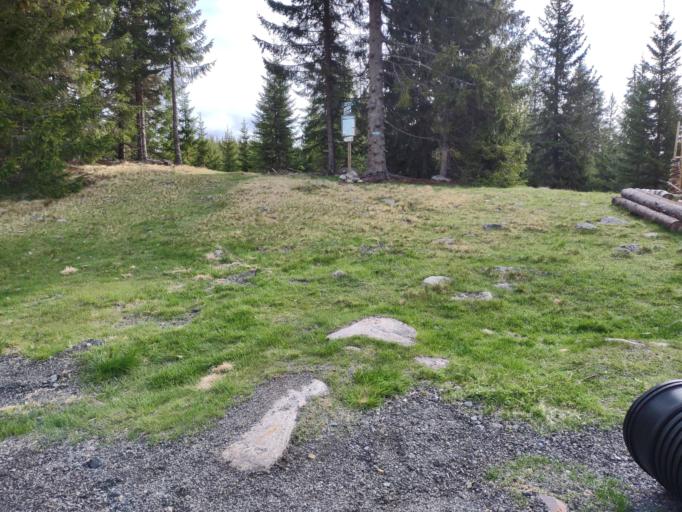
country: NO
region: Oppland
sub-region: Lunner
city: Grua
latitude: 60.2734
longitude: 10.7583
